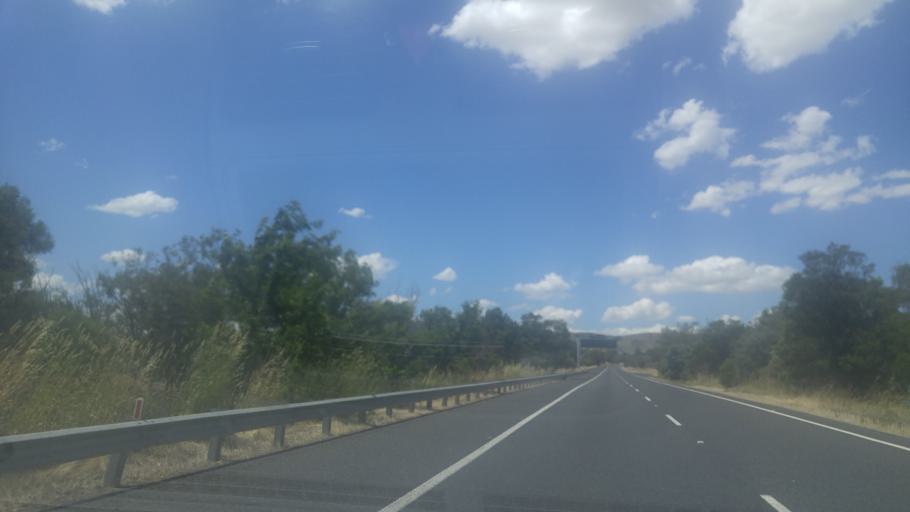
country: AU
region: New South Wales
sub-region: Yass Valley
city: Yass
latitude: -34.7855
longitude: 148.7041
